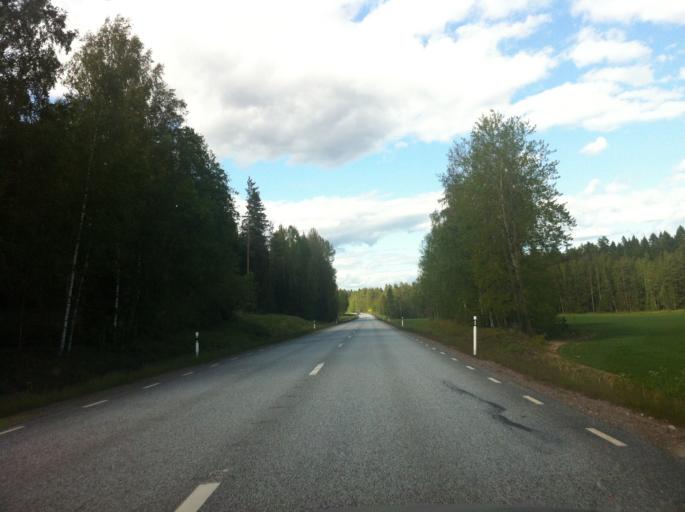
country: SE
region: Vaermland
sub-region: Storfors Kommun
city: Storfors
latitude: 59.4573
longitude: 14.2483
